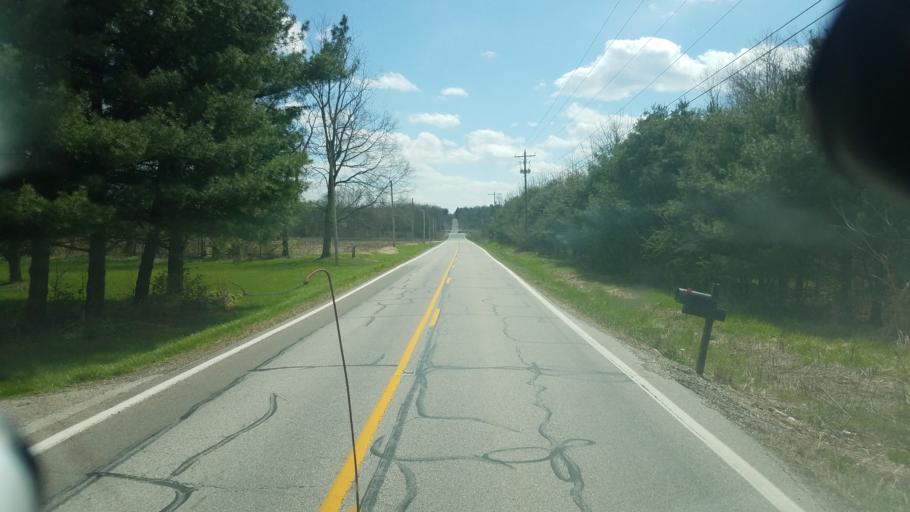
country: US
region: Ohio
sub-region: Licking County
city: Johnstown
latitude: 40.1192
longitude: -82.6603
